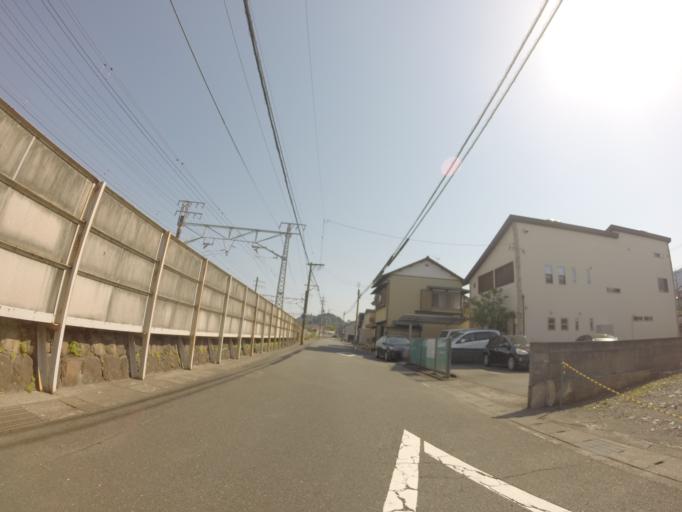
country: JP
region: Shizuoka
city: Fuji
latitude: 35.1442
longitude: 138.6191
